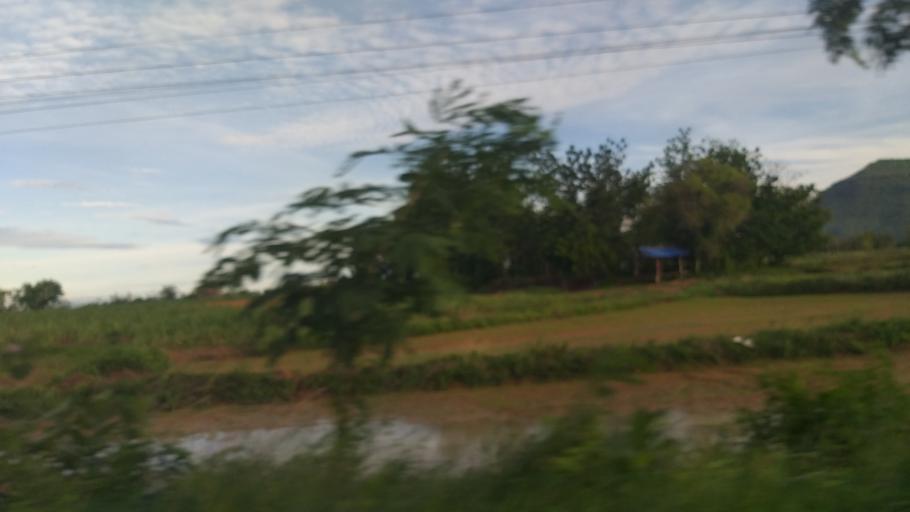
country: TH
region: Chaiyaphum
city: Ban Thaen
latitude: 16.3488
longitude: 102.2419
